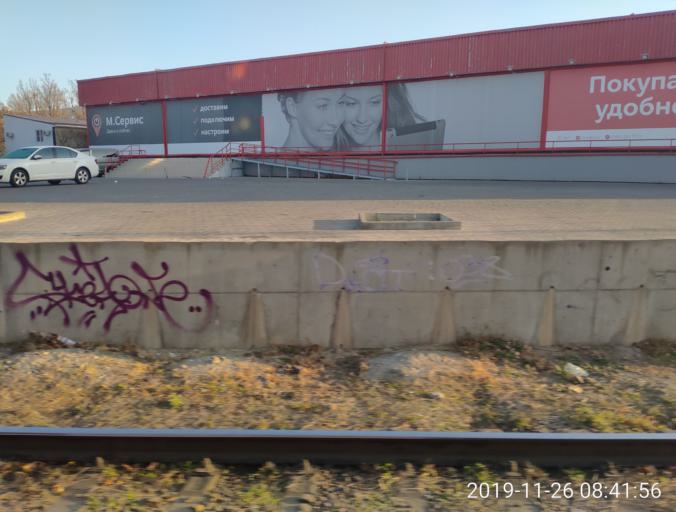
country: RU
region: Krasnodarskiy
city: Krasnodar
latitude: 45.0527
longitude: 38.9845
